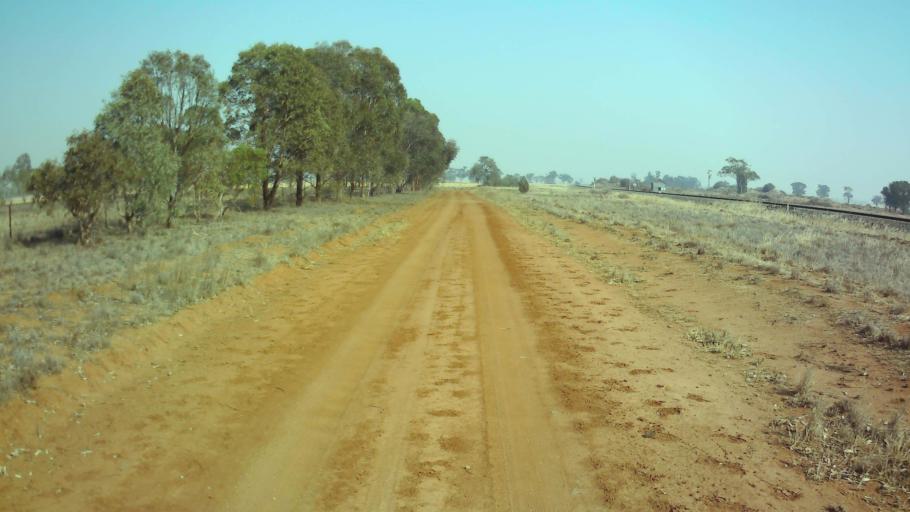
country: AU
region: New South Wales
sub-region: Weddin
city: Grenfell
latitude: -34.0040
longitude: 147.7892
